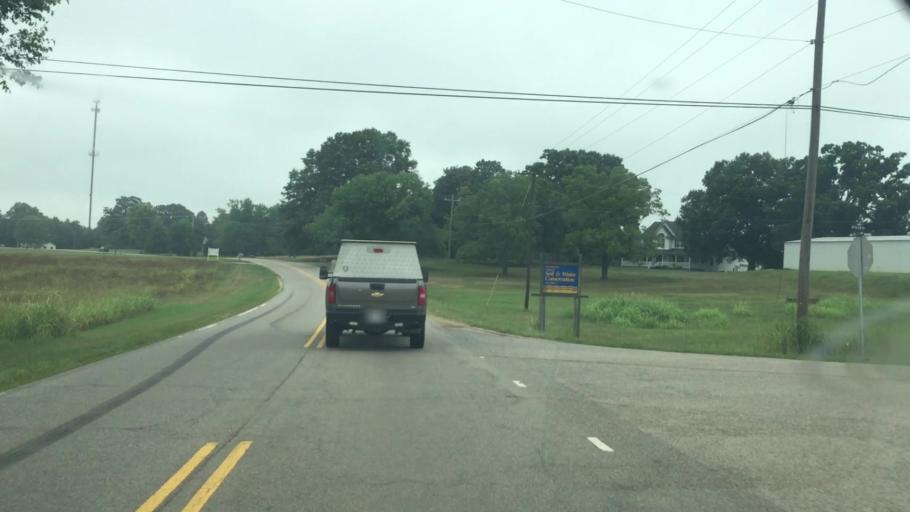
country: US
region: North Carolina
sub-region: Gaston County
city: Davidson
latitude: 35.4988
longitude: -80.7698
